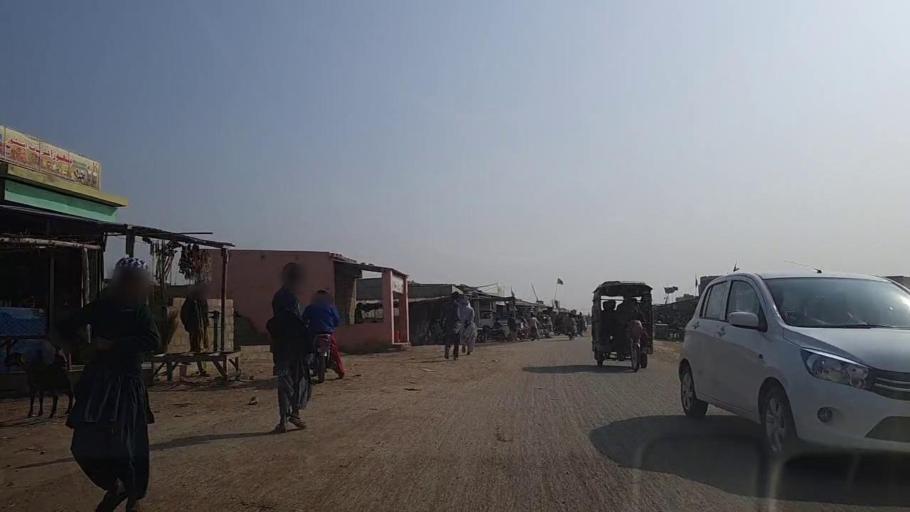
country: PK
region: Sindh
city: Keti Bandar
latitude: 24.2384
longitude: 67.6074
